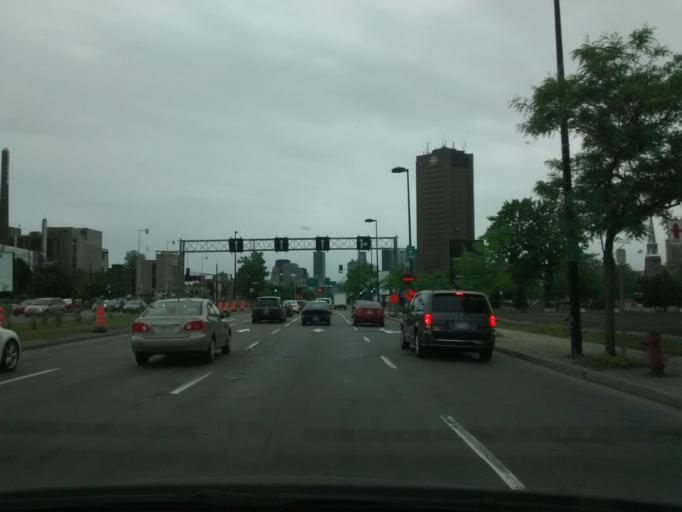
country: CA
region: Quebec
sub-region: Monteregie
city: Longueuil
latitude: 45.5215
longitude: -73.5473
